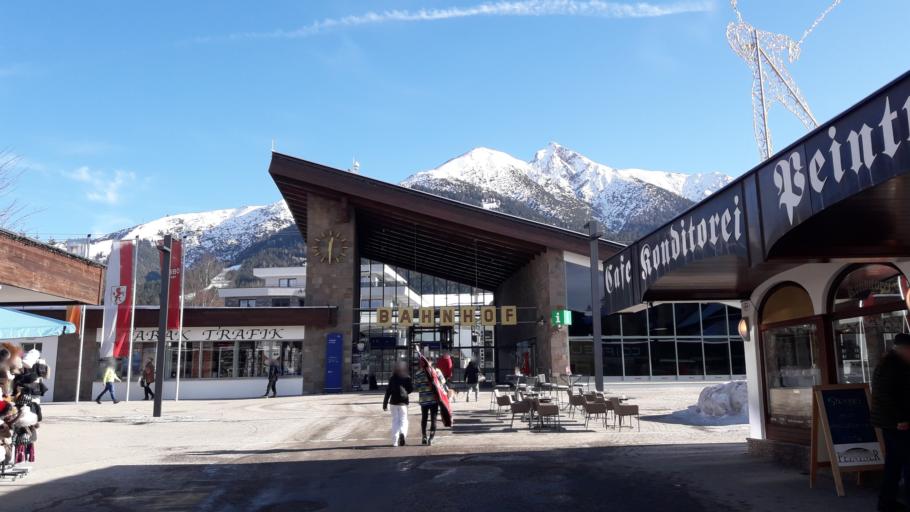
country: AT
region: Tyrol
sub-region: Politischer Bezirk Innsbruck Land
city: Seefeld in Tirol
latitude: 47.3289
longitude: 11.1886
